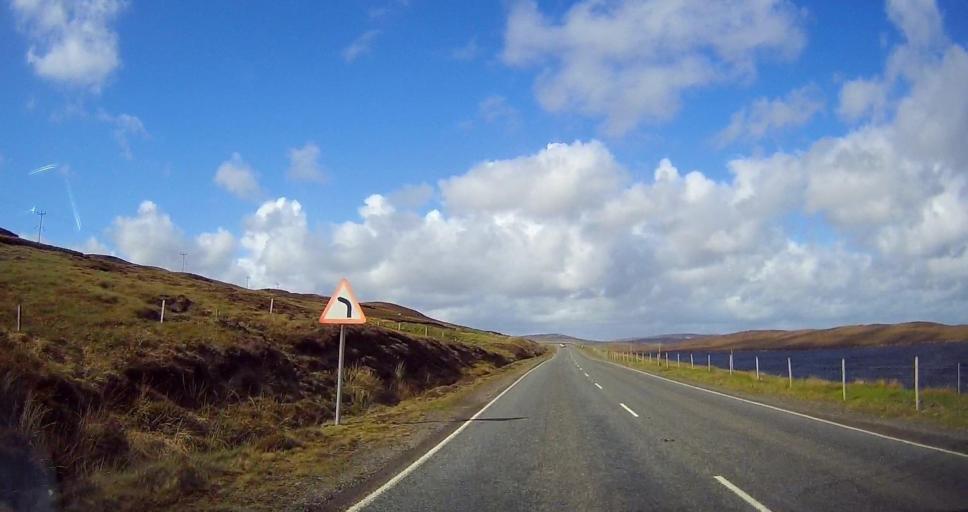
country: GB
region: Scotland
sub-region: Shetland Islands
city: Lerwick
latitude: 60.2472
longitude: -1.2276
